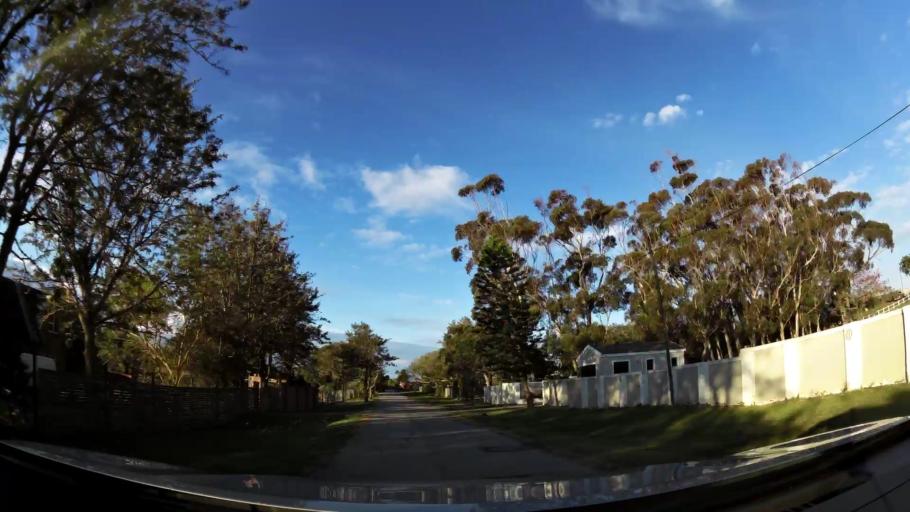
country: ZA
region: Eastern Cape
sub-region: Nelson Mandela Bay Metropolitan Municipality
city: Port Elizabeth
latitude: -33.9759
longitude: 25.4873
